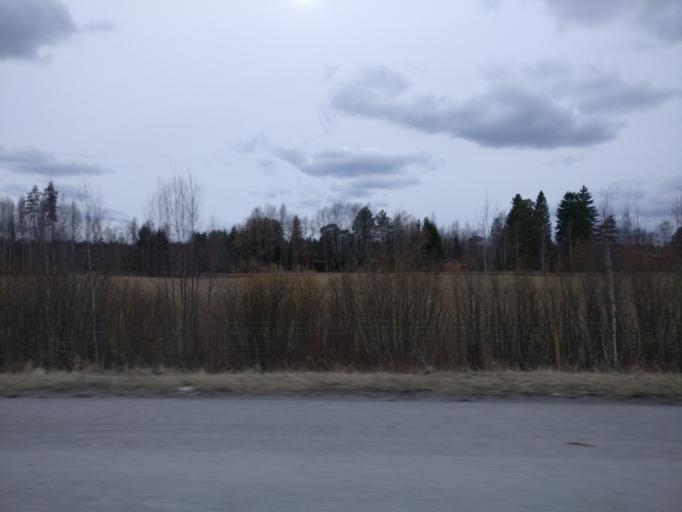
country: FI
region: Haeme
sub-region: Haemeenlinna
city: Janakkala
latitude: 60.8624
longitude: 24.5848
